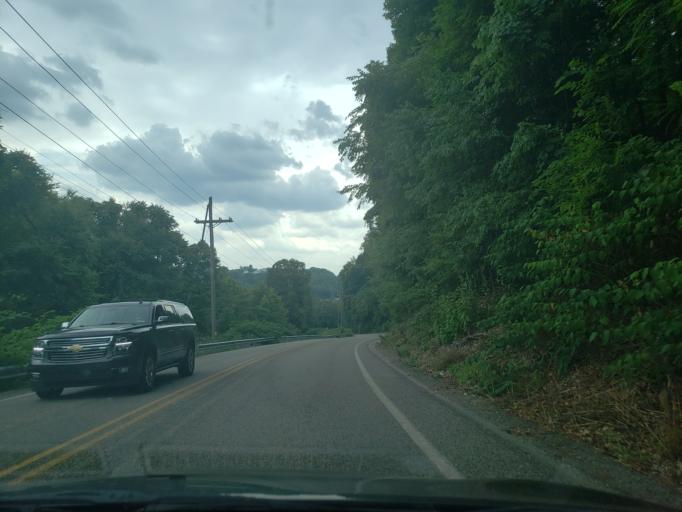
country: US
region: Pennsylvania
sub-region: Allegheny County
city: Avalon
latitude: 40.5099
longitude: -80.0672
